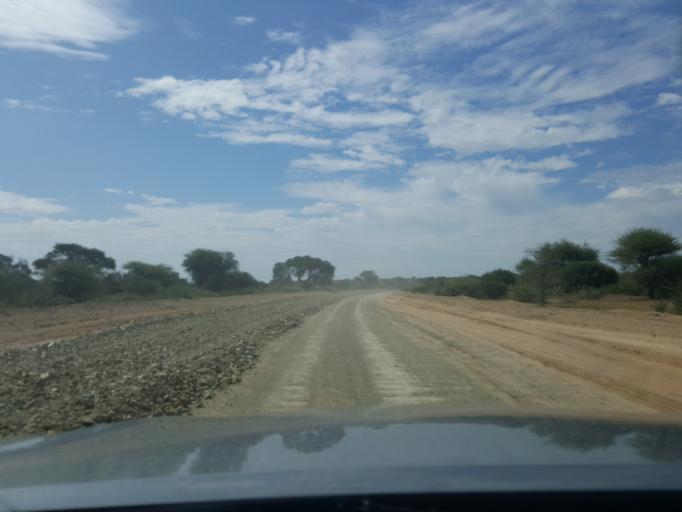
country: BW
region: Kweneng
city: Letlhakeng
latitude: -23.9953
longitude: 24.9713
